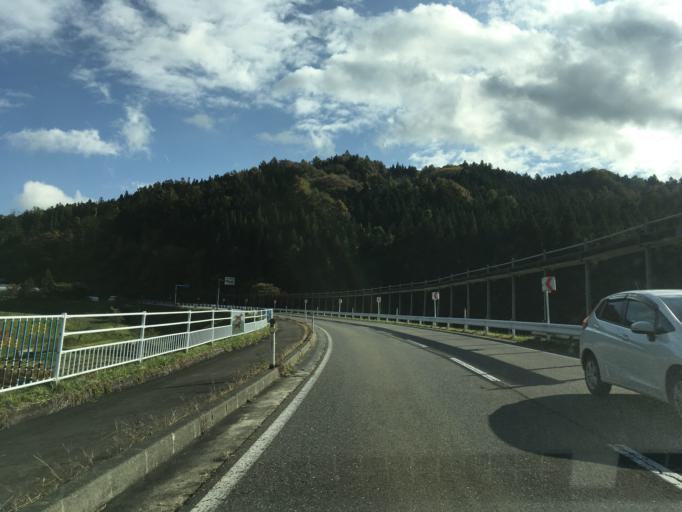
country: JP
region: Iwate
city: Tono
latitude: 39.3641
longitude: 141.4010
